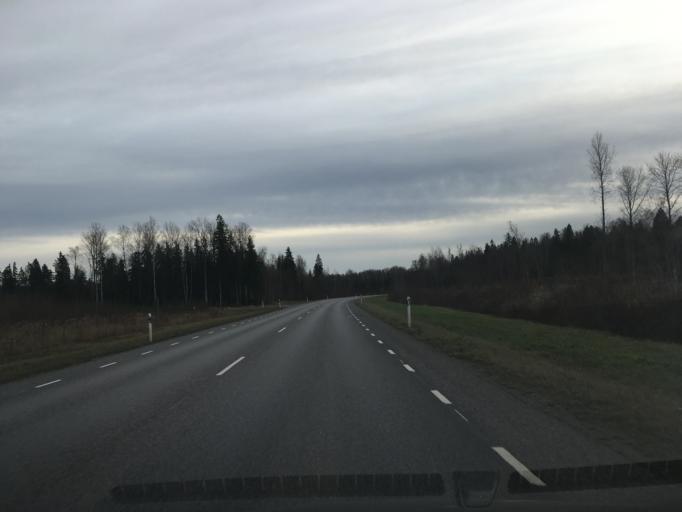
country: EE
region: Ida-Virumaa
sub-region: Johvi vald
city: Johvi
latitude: 59.3542
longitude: 27.4663
